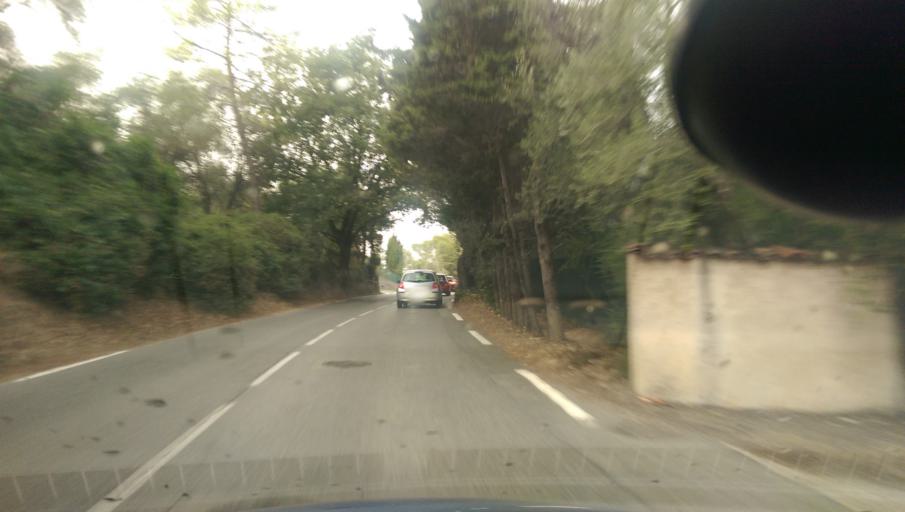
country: FR
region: Provence-Alpes-Cote d'Azur
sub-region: Departement des Alpes-Maritimes
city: Valbonne
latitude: 43.6424
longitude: 7.0262
